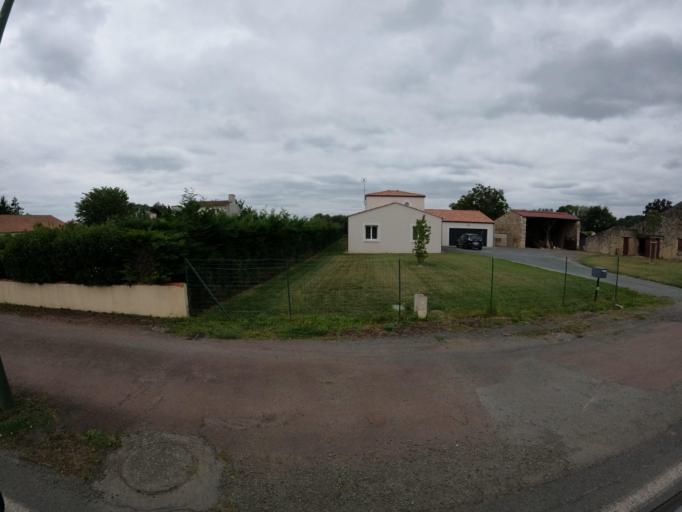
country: FR
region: Pays de la Loire
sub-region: Departement de la Vendee
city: Sainte-Hermine
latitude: 46.5606
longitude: -1.0609
